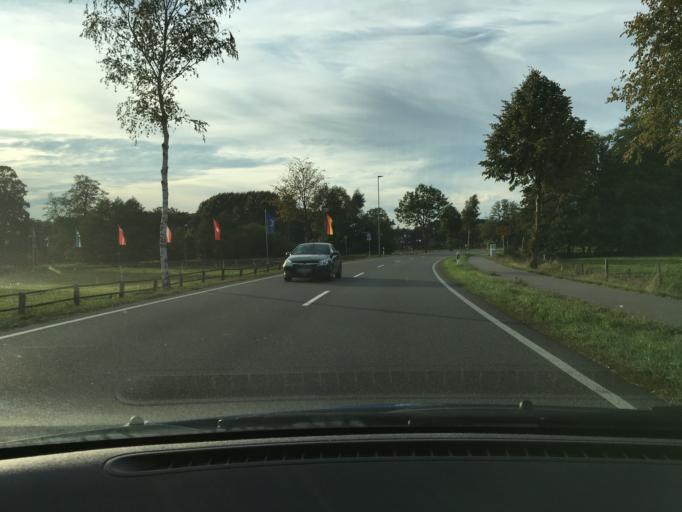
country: DE
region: Lower Saxony
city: Soltau
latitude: 52.9896
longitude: 9.9119
